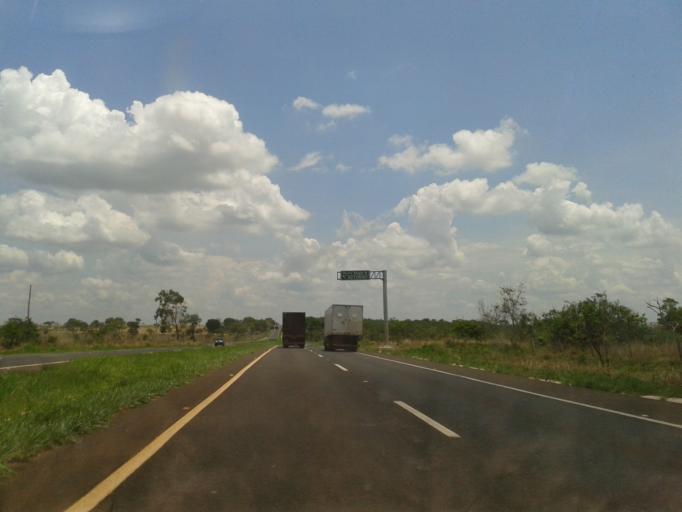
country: BR
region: Minas Gerais
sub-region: Monte Alegre De Minas
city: Monte Alegre de Minas
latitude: -18.8514
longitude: -48.7939
